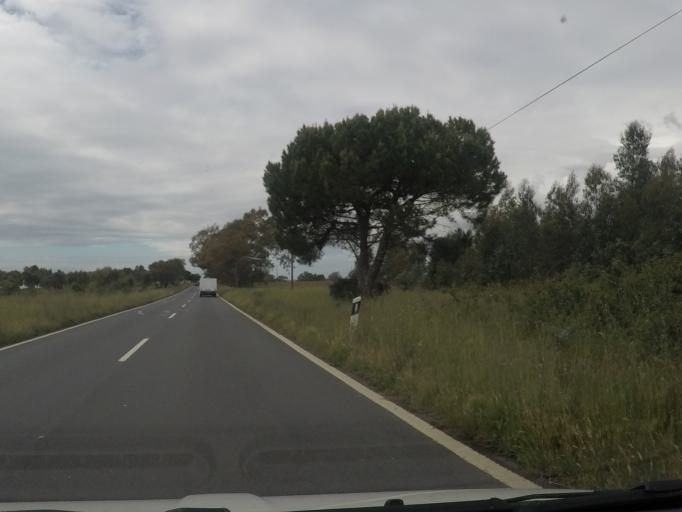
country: PT
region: Setubal
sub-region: Sines
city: Porto Covo
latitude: 37.8854
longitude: -8.7527
